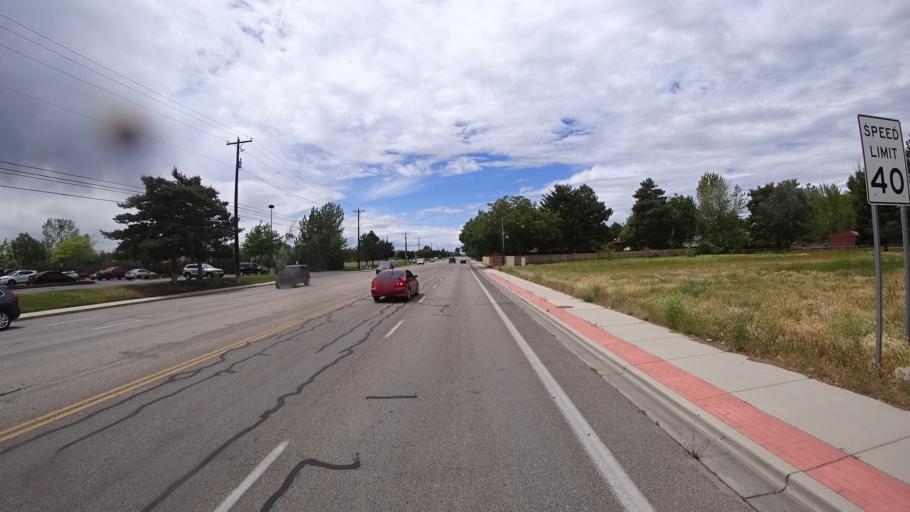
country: US
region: Idaho
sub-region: Ada County
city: Meridian
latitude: 43.5903
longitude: -116.3173
